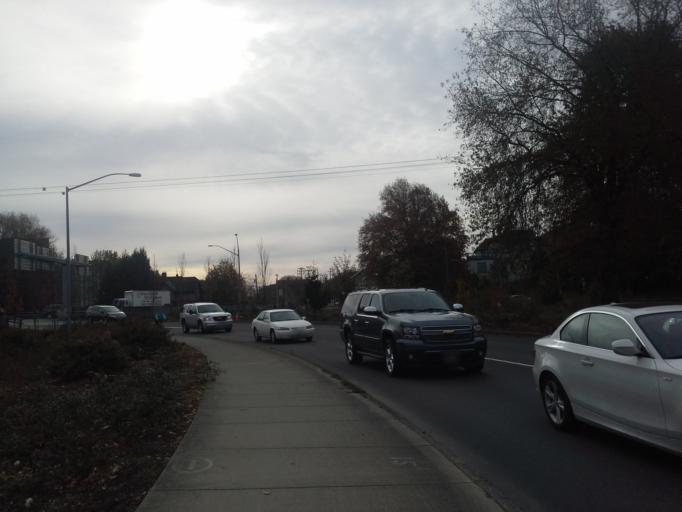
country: US
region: Oregon
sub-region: Multnomah County
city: Portland
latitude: 45.5012
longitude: -122.6752
